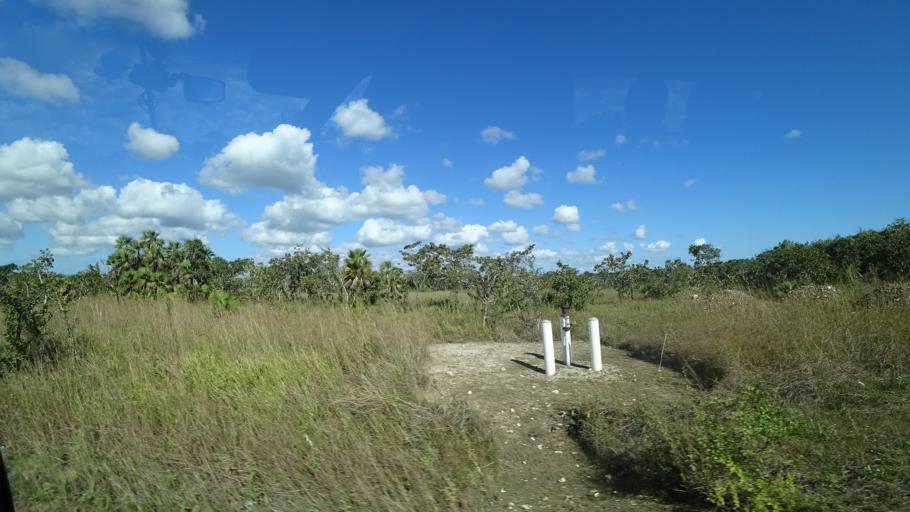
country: BZ
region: Belize
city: Belize City
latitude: 17.5809
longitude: -88.3774
